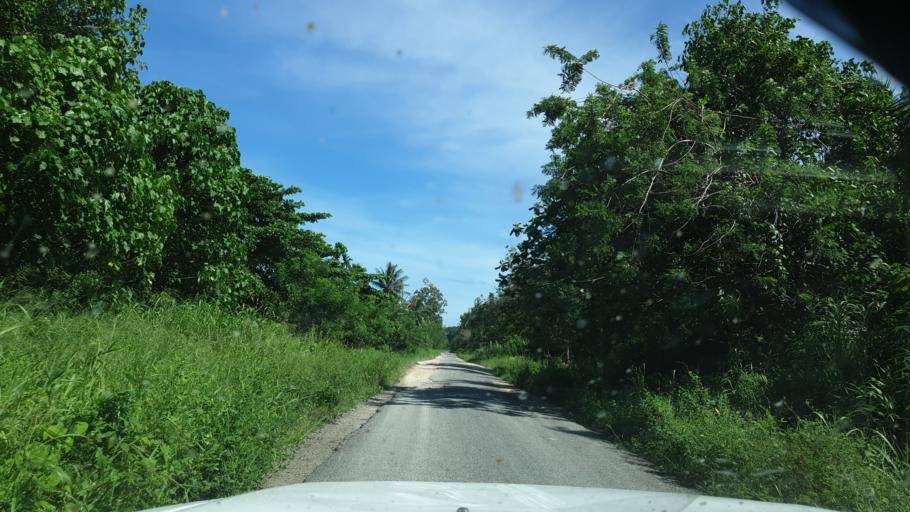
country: PG
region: Madang
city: Madang
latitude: -4.6869
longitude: 145.6021
